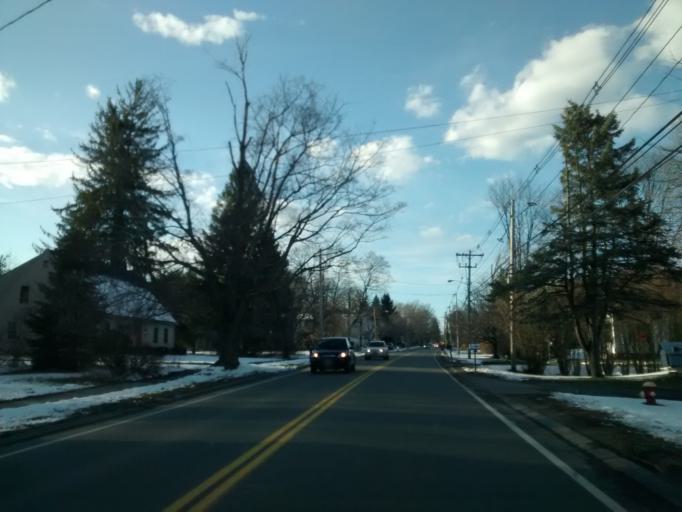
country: US
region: Massachusetts
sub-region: Middlesex County
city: Hopkinton
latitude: 42.2039
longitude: -71.5103
